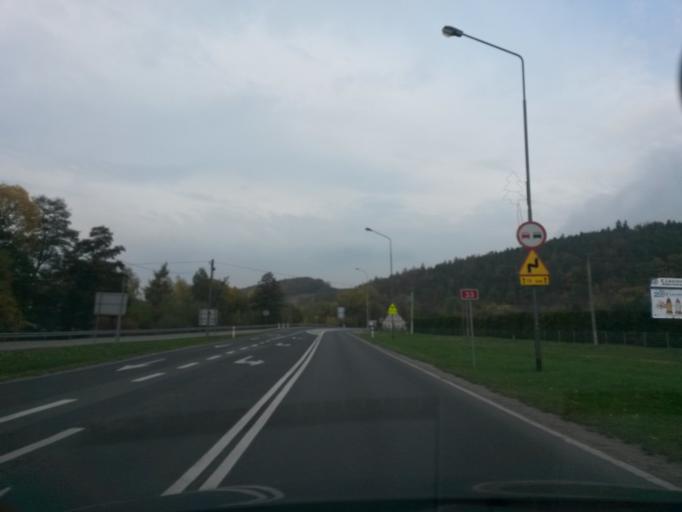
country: PL
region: Lower Silesian Voivodeship
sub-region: Powiat klodzki
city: Klodzko
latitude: 50.3730
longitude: 16.6744
